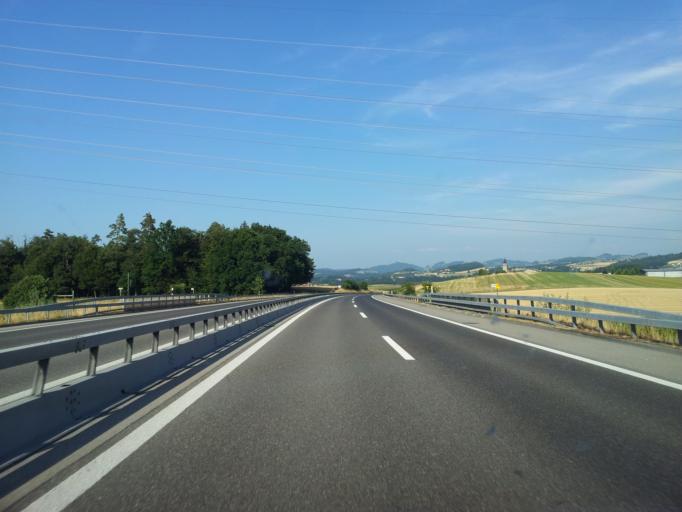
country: CH
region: Fribourg
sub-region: Sense District
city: Schmitten
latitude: 46.8741
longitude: 7.2609
